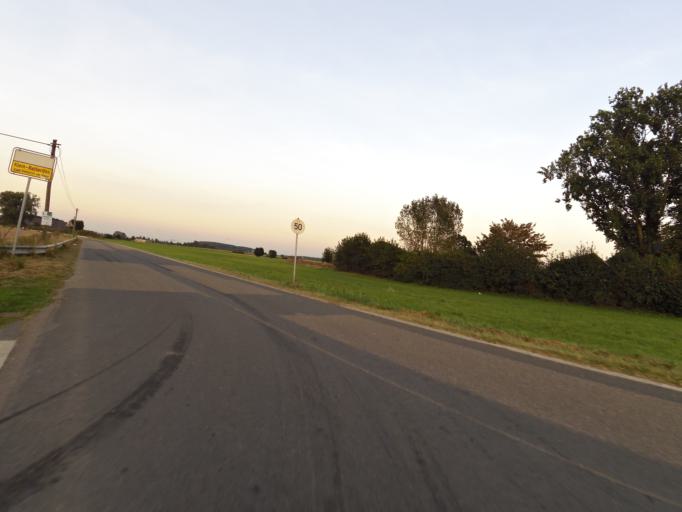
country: DE
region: North Rhine-Westphalia
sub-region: Regierungsbezirk Dusseldorf
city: Emmerich
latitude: 51.8544
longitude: 6.2634
